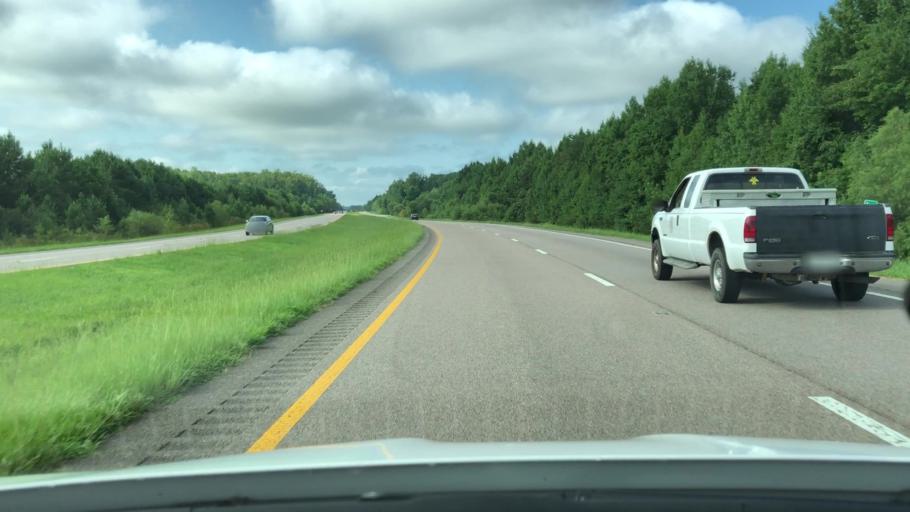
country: US
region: Virginia
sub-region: City of Portsmouth
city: Portsmouth Heights
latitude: 36.6423
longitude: -76.3617
